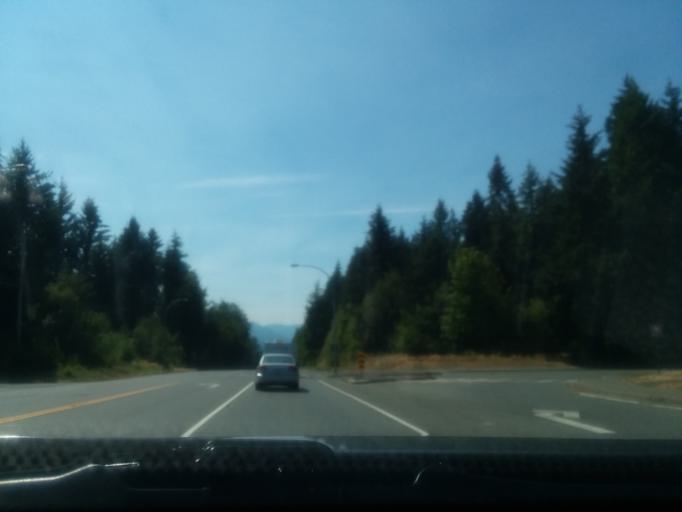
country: CA
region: British Columbia
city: Courtenay
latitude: 49.7082
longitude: -124.9700
